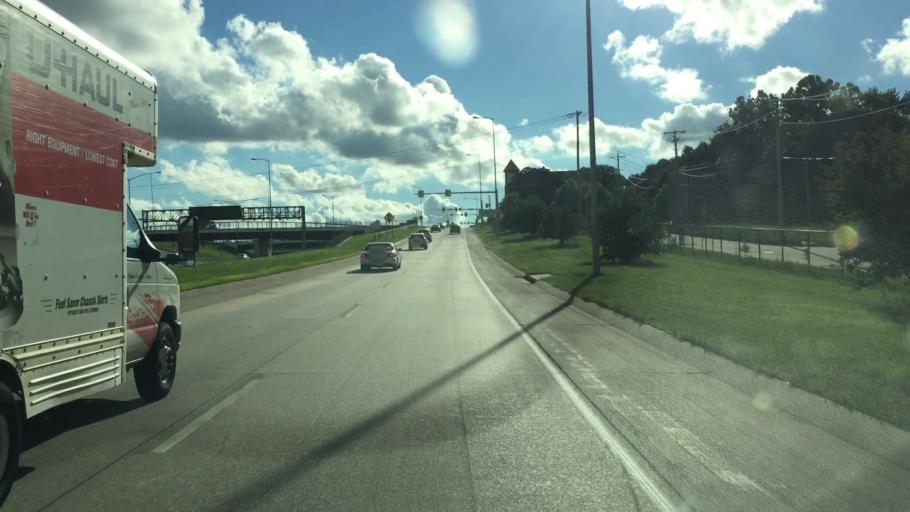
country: US
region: Iowa
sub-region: Polk County
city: Des Moines
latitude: 41.5964
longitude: -93.6395
